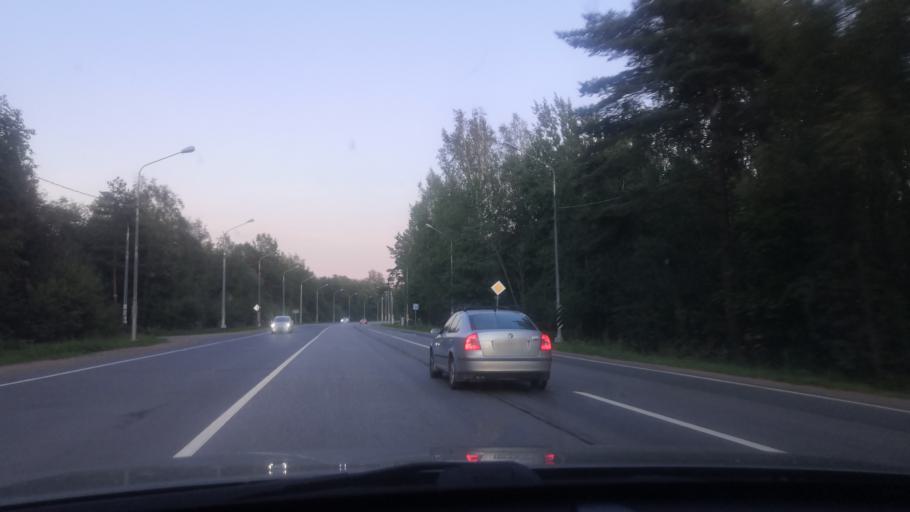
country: RU
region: St.-Petersburg
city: Beloostrov
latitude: 60.1958
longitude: 30.0609
